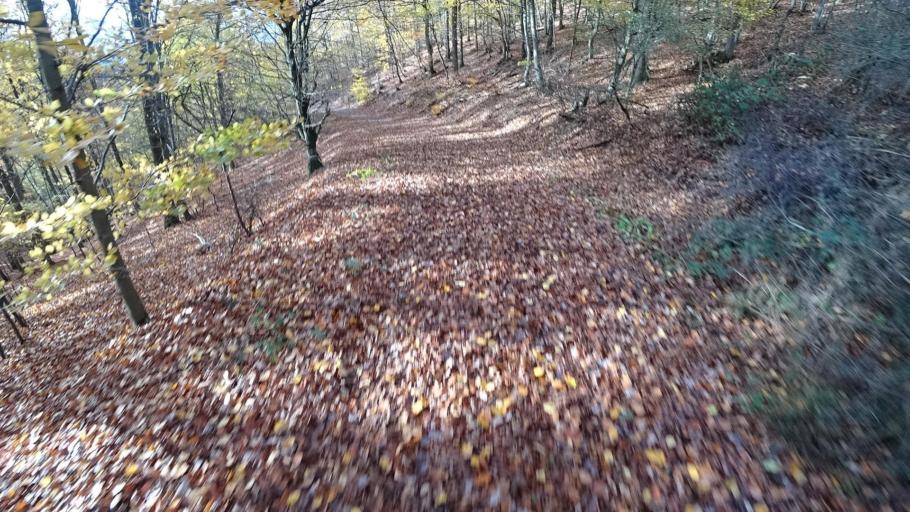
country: DE
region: Rheinland-Pfalz
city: Lind
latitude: 50.4890
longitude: 6.9254
